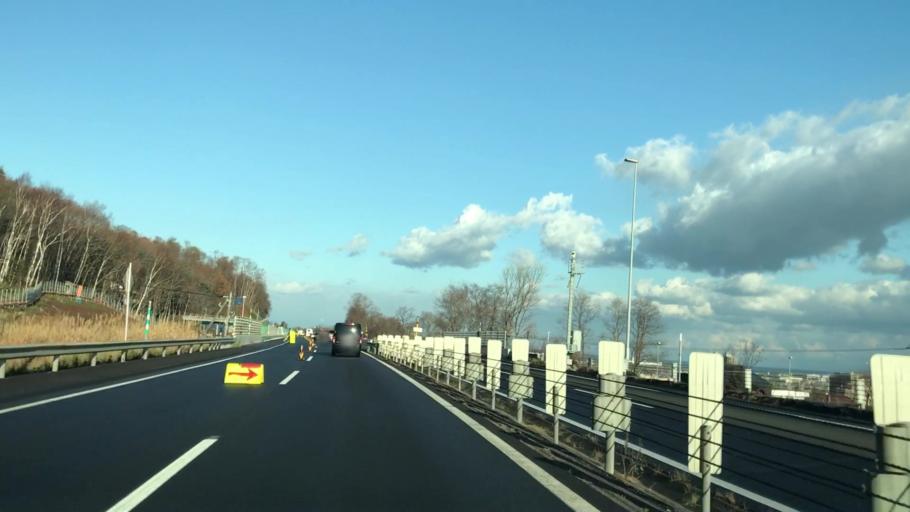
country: JP
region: Hokkaido
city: Sapporo
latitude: 43.1102
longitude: 141.2401
